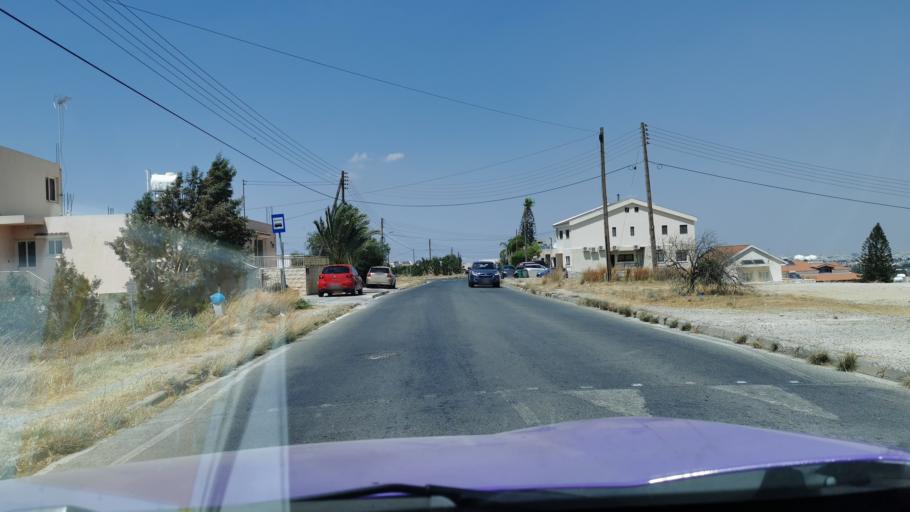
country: CY
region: Lefkosia
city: Kato Deftera
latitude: 35.1198
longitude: 33.2928
